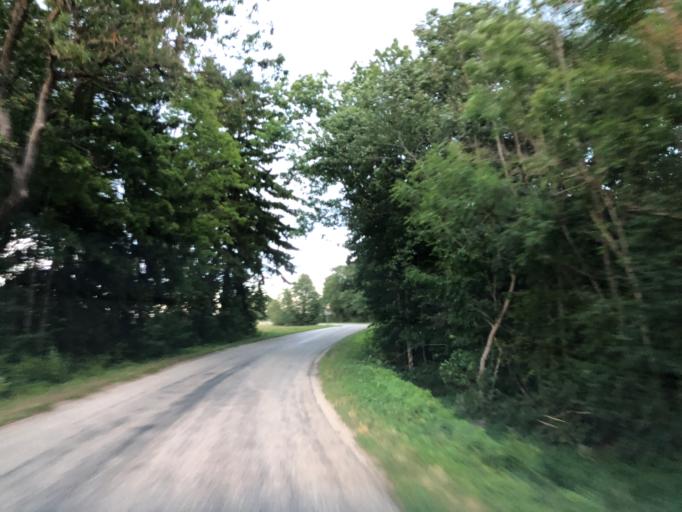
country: EE
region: Laeaene
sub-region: Ridala Parish
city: Uuemoisa
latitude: 58.8807
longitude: 23.6446
